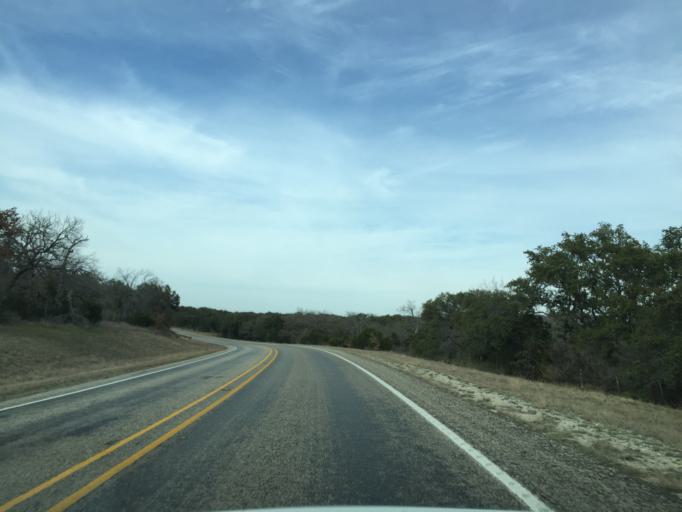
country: US
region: Texas
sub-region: Llano County
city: Llano
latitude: 30.4901
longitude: -98.7034
